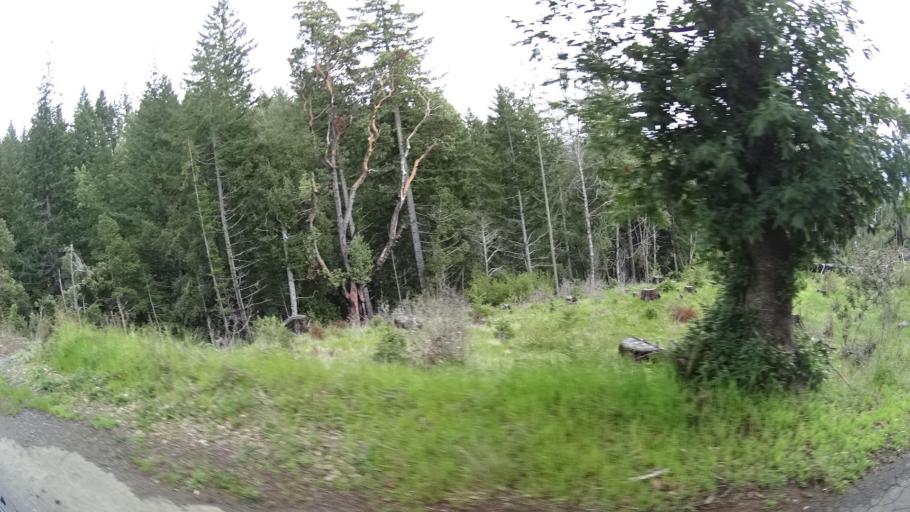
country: US
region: California
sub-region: Humboldt County
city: Blue Lake
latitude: 40.8592
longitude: -123.9094
